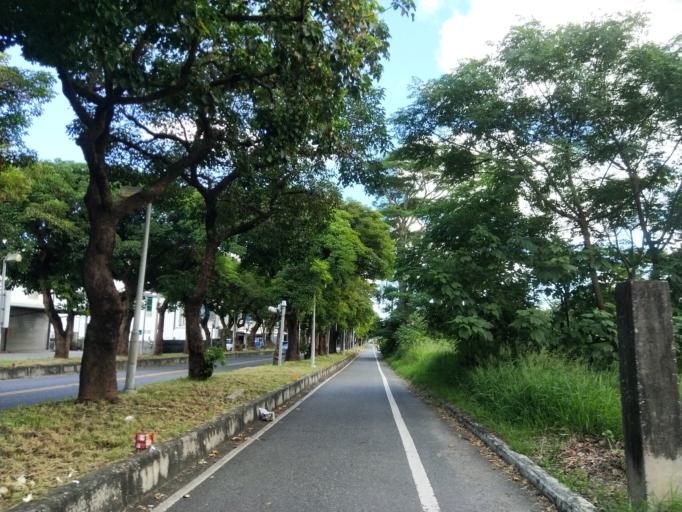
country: TW
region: Taiwan
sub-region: Taitung
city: Taitung
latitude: 22.7925
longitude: 121.1060
